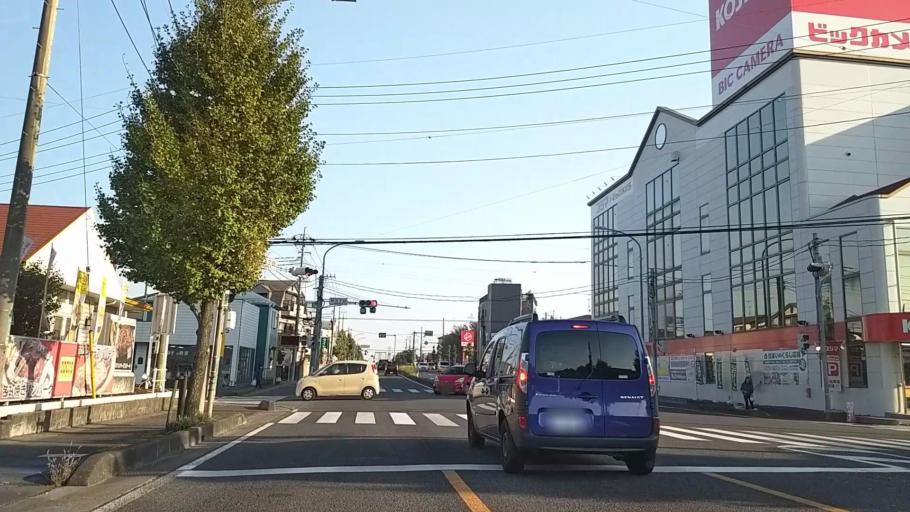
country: JP
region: Saitama
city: Sayama
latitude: 35.8086
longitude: 139.4044
